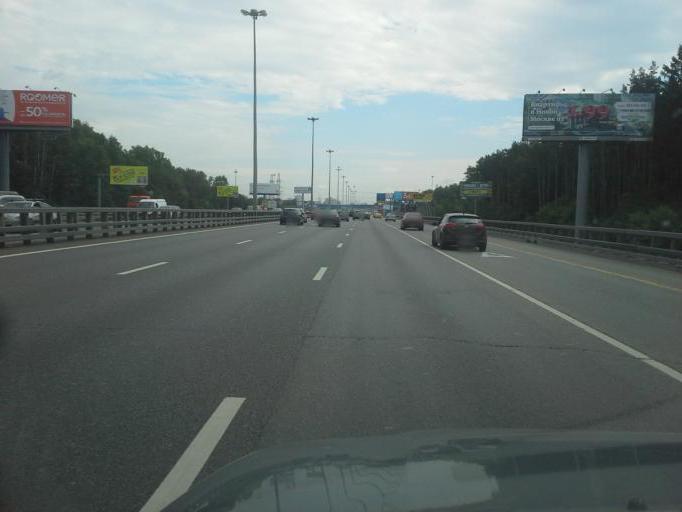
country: RU
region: Moscow
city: Solntsevo
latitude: 55.6247
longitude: 37.4147
